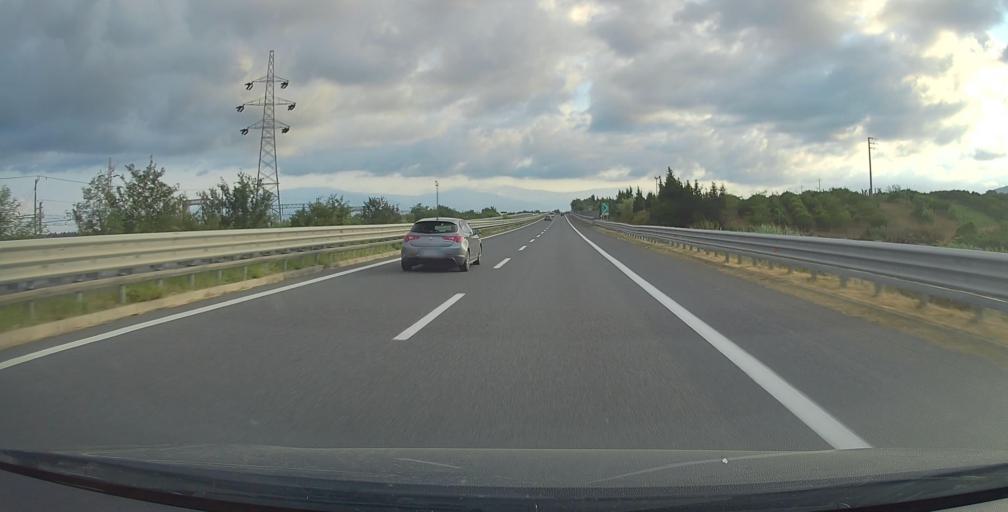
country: IT
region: Calabria
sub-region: Provincia di Catanzaro
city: Acconia
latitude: 38.8104
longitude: 16.2338
